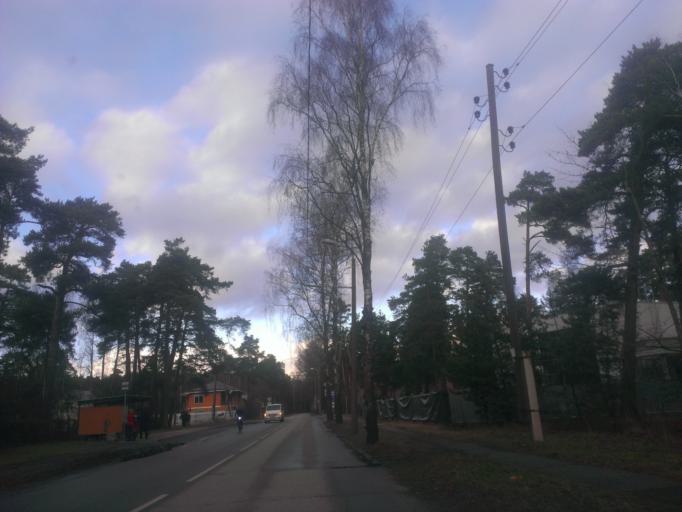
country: LV
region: Riga
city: Bolderaja
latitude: 57.0699
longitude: 24.1051
